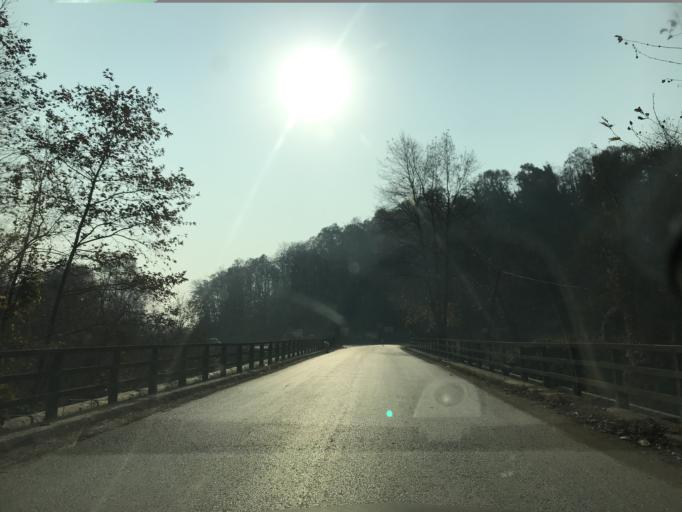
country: TR
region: Duzce
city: Cumayeri
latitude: 40.8951
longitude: 30.9559
